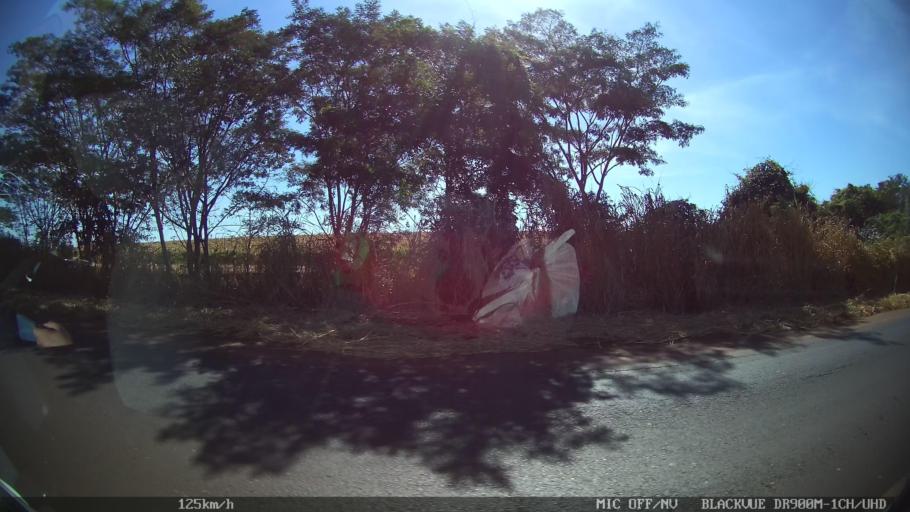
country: BR
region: Sao Paulo
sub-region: Barretos
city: Barretos
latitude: -20.4624
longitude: -48.4699
